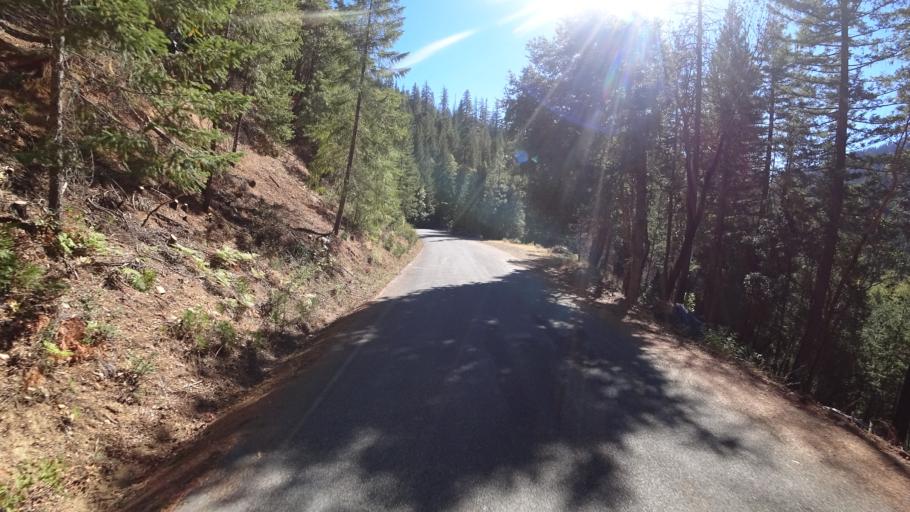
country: US
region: California
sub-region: Siskiyou County
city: Yreka
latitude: 41.3600
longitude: -123.0316
